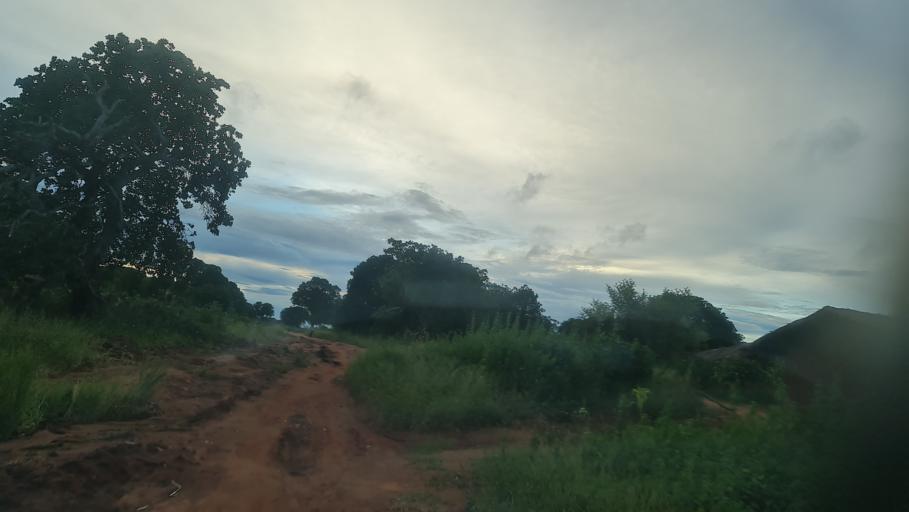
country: MZ
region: Nampula
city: Nacala
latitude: -14.7406
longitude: 39.9391
